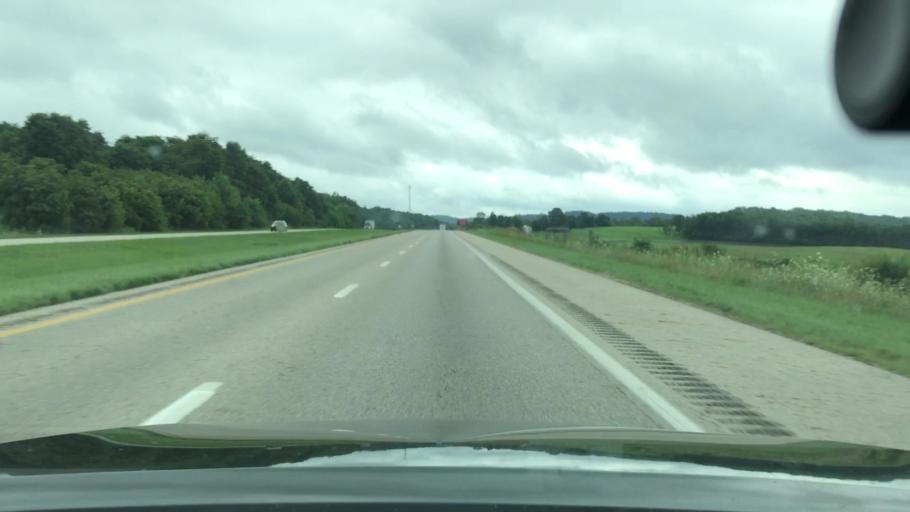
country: US
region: Ohio
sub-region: Ross County
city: Chillicothe
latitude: 39.2616
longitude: -82.8654
